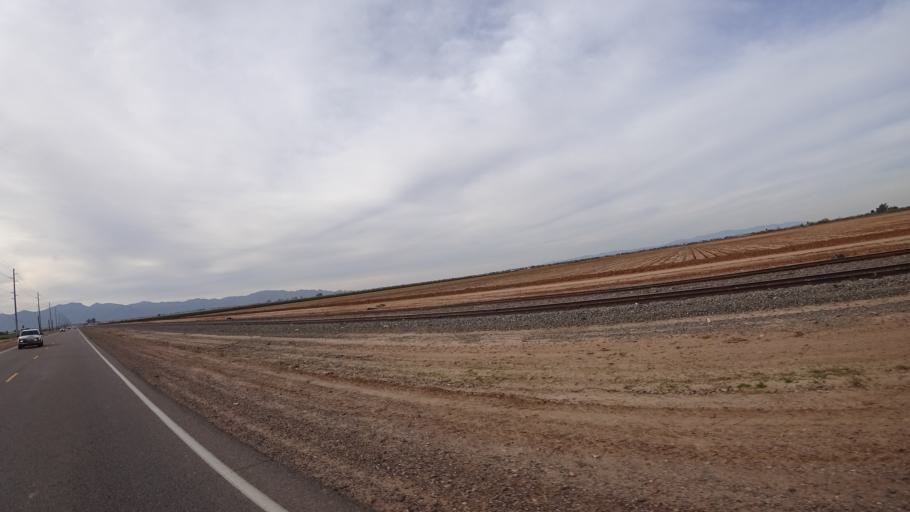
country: US
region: Arizona
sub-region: Maricopa County
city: Citrus Park
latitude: 33.5659
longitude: -112.3828
